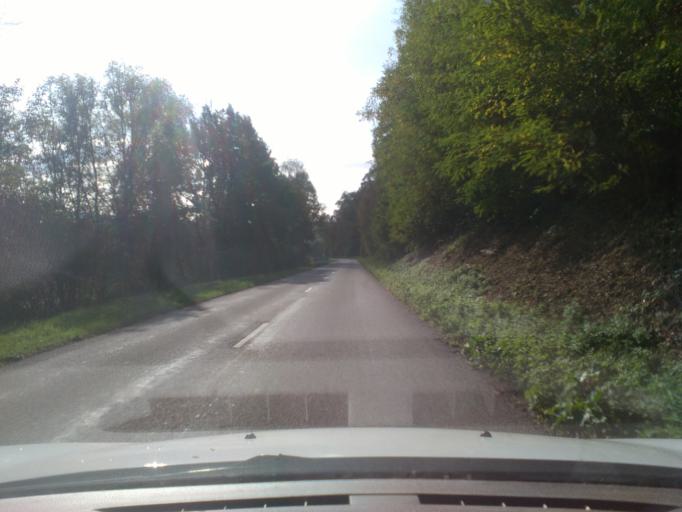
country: FR
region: Lorraine
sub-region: Departement des Vosges
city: Ban-de-Laveline
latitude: 48.2870
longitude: 7.0554
